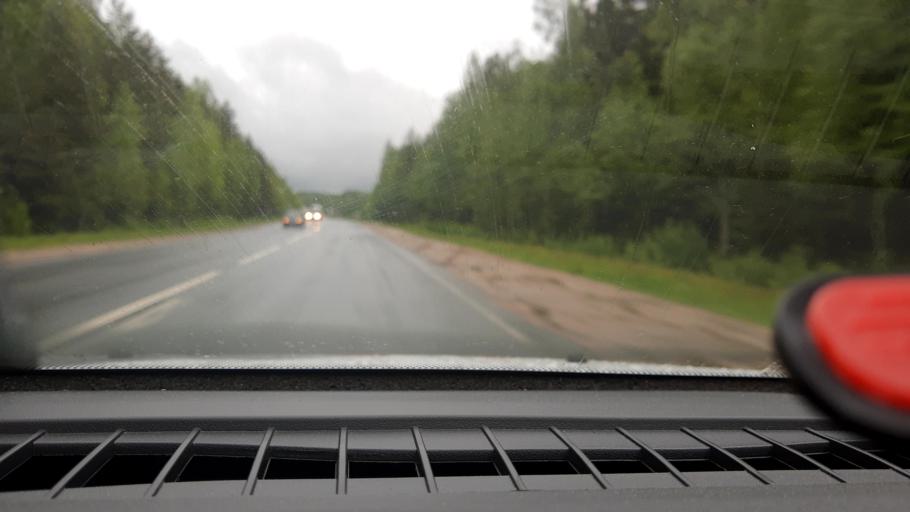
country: RU
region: Nizjnij Novgorod
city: Semenov
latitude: 56.7674
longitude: 44.4102
